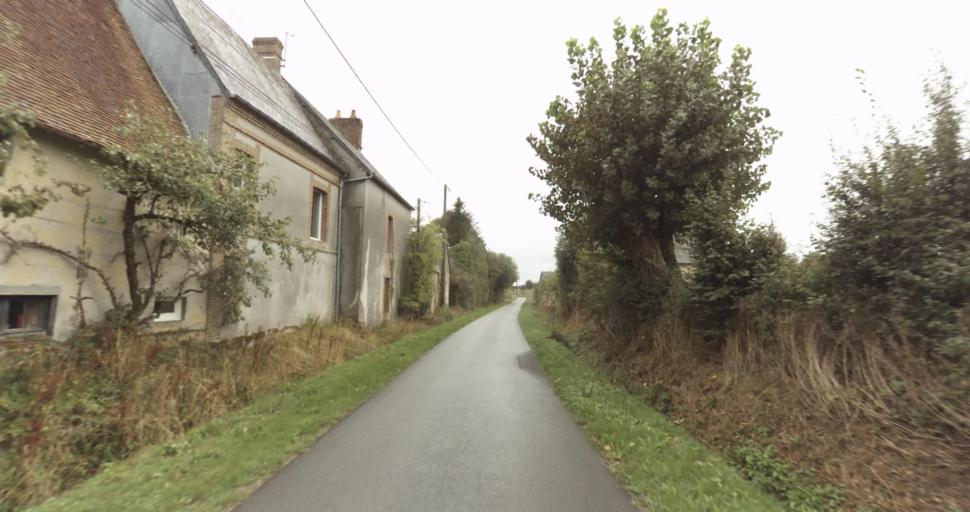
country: FR
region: Lower Normandy
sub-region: Departement de l'Orne
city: Sainte-Gauburge-Sainte-Colombe
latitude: 48.7467
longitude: 0.4520
